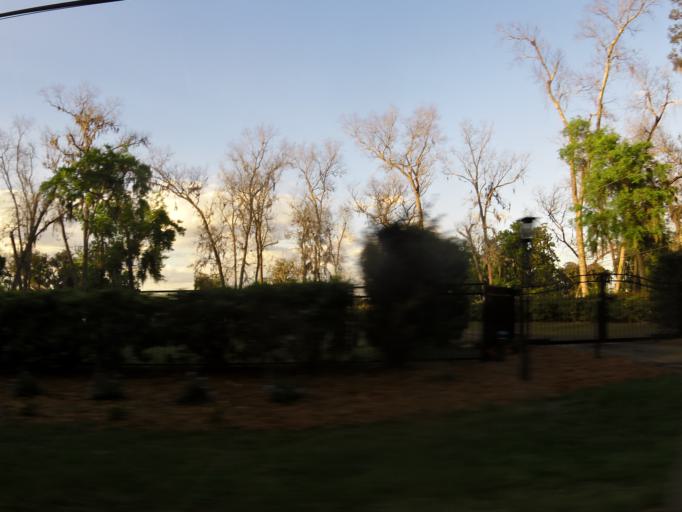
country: US
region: Florida
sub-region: Saint Johns County
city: Fruit Cove
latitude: 30.1276
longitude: -81.6014
